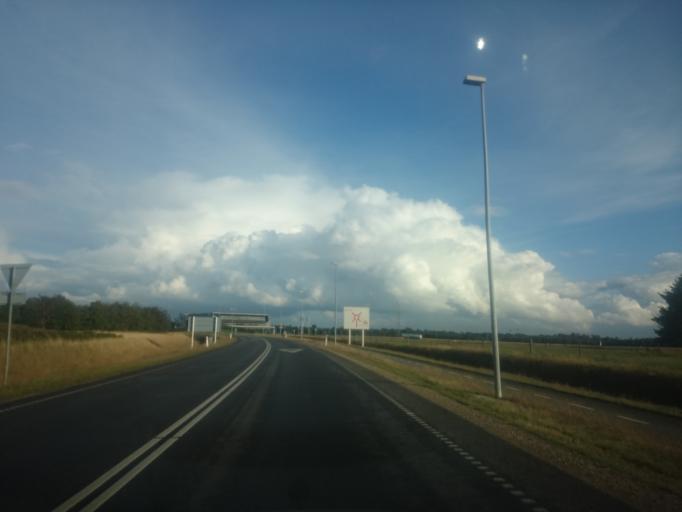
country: DK
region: South Denmark
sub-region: Billund Kommune
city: Billund
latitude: 55.7379
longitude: 9.0920
